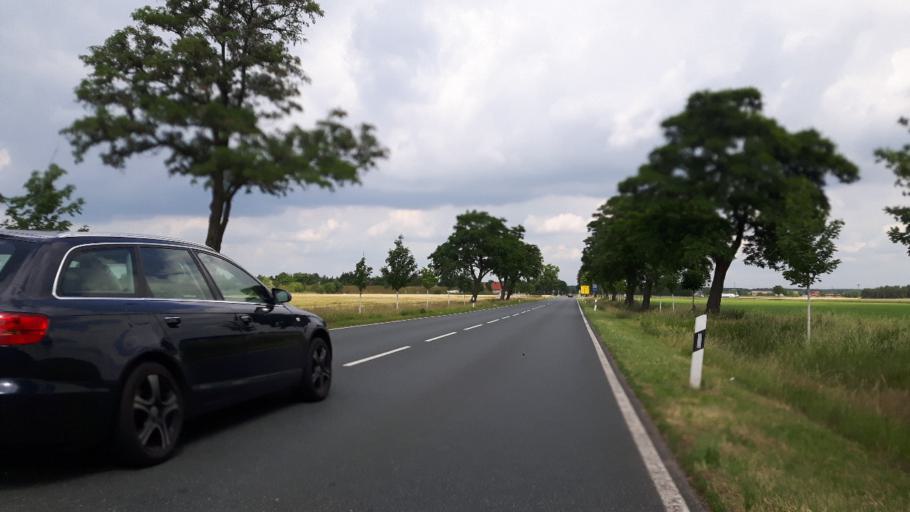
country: DE
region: Saxony-Anhalt
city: Schlaitz
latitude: 51.6536
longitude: 12.4370
